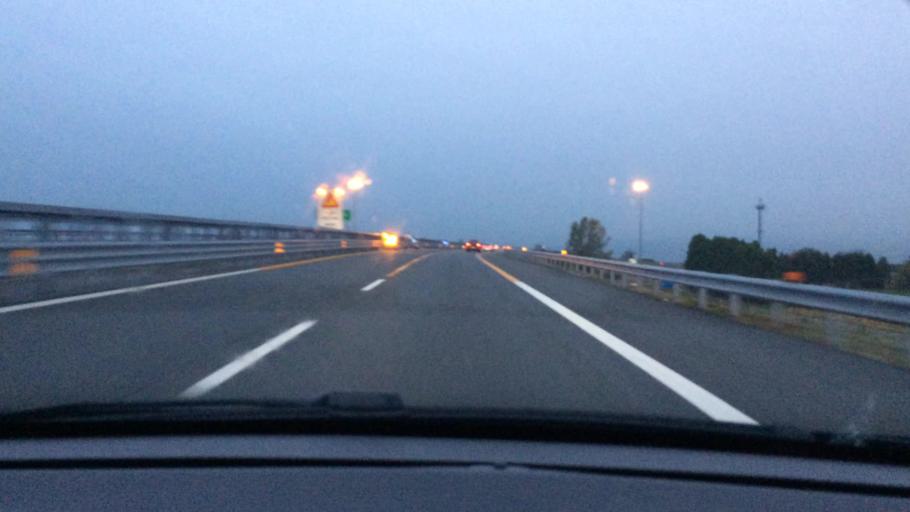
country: IT
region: Piedmont
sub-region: Provincia di Torino
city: Orbassano
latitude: 44.9828
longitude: 7.5538
